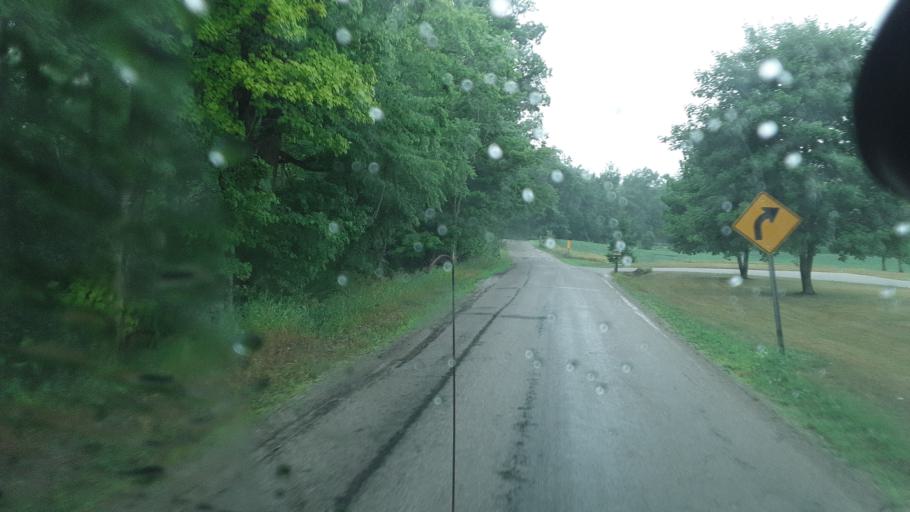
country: US
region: Indiana
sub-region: DeKalb County
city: Butler
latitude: 41.4276
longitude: -84.8105
